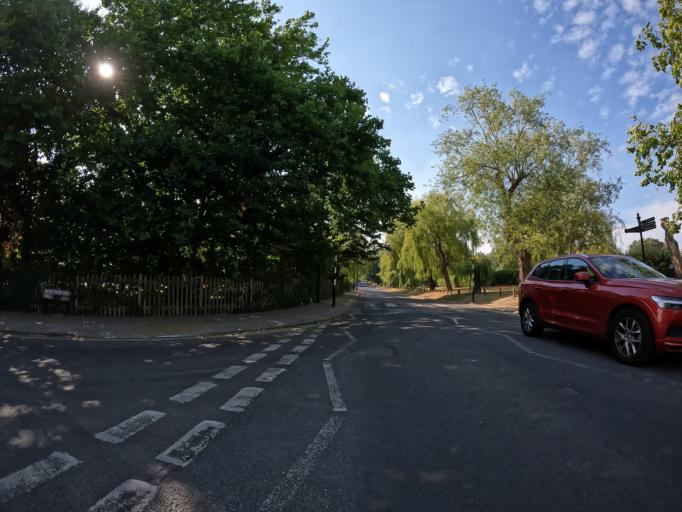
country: GB
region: England
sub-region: Hertfordshire
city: Potters Bar
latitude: 51.6855
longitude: -0.1601
